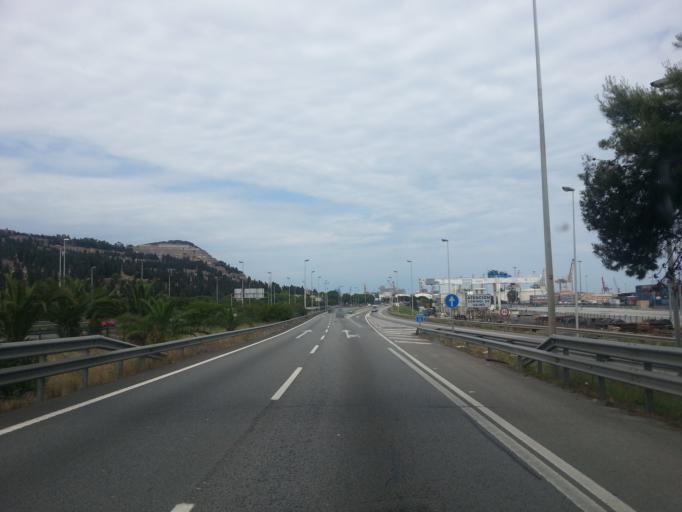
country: ES
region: Catalonia
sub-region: Provincia de Barcelona
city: Sants-Montjuic
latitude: 41.3497
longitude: 2.1483
